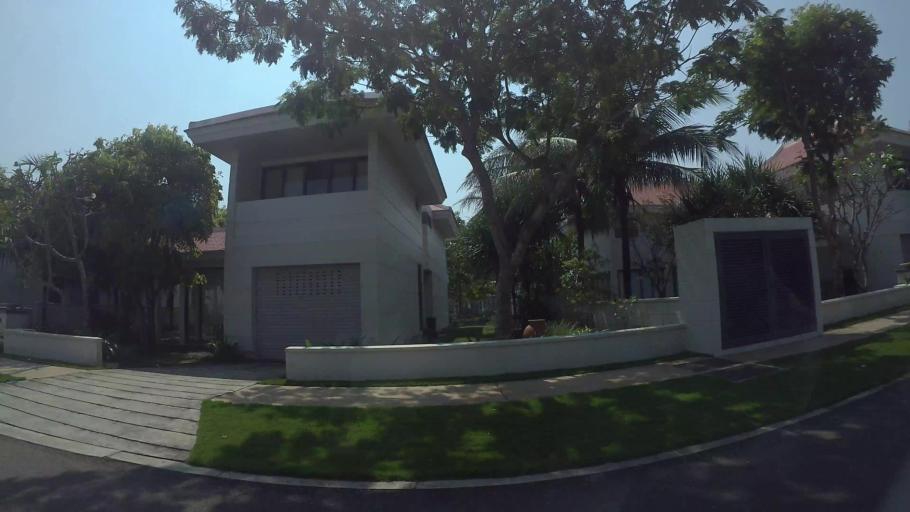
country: VN
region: Da Nang
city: Ngu Hanh Son
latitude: 15.9779
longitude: 108.2823
